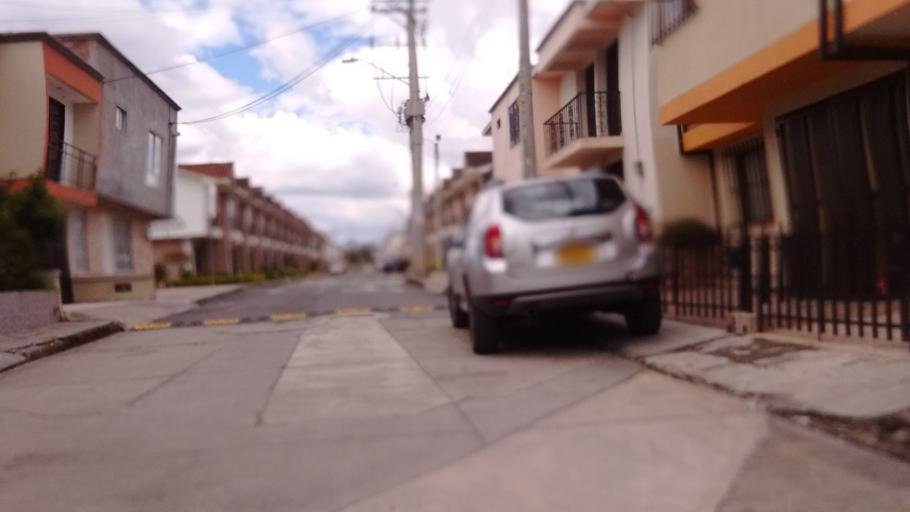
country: CO
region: Cauca
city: Popayan
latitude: 2.4615
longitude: -76.5867
